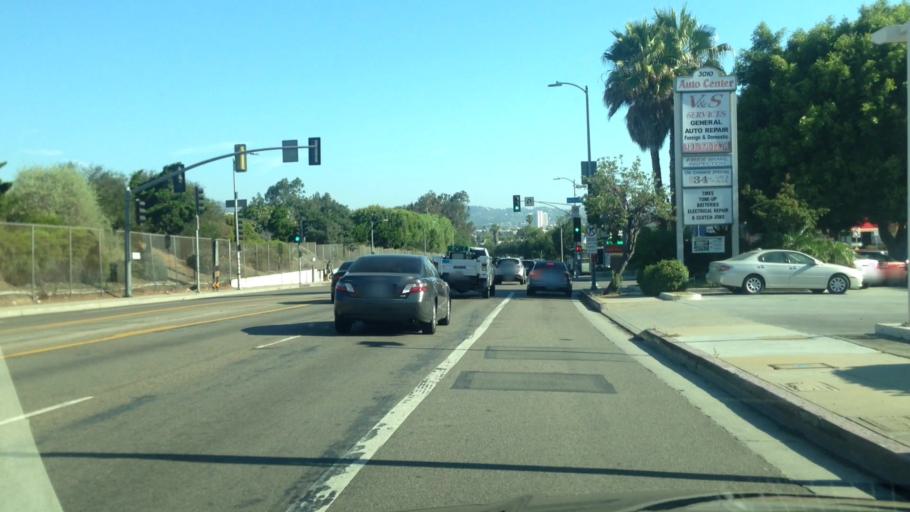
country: US
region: California
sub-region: Los Angeles County
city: Westwood, Los Angeles
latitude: 34.0195
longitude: -118.4448
